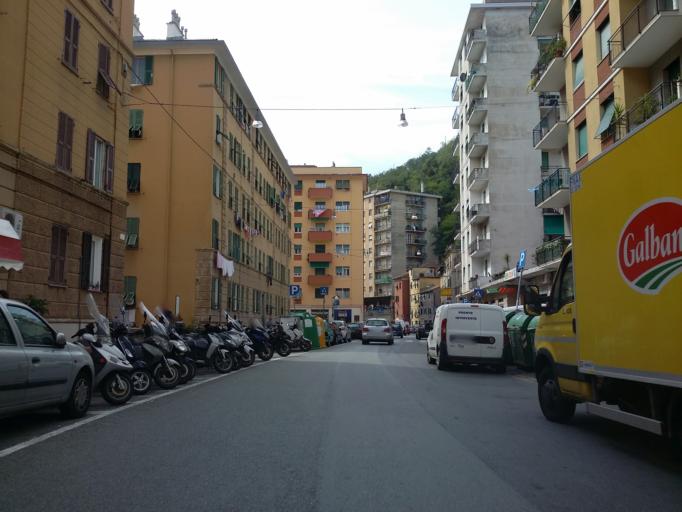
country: IT
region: Liguria
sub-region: Provincia di Genova
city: Piccarello
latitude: 44.4442
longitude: 8.9649
